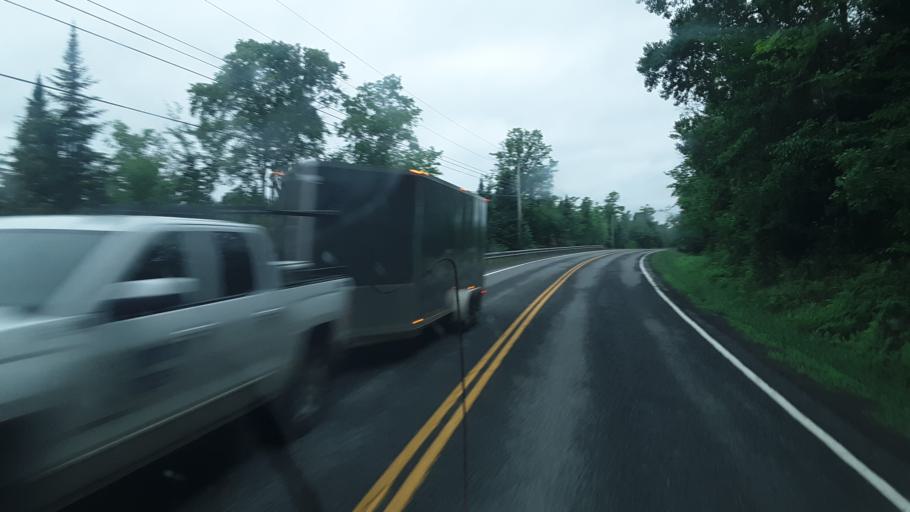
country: US
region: Maine
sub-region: Penobscot County
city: Patten
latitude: 46.1631
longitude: -68.3456
